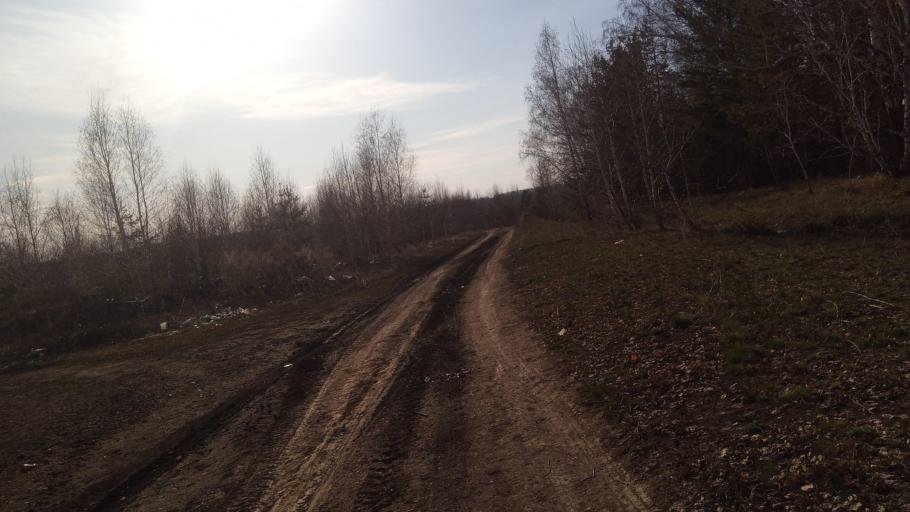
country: RU
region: Chelyabinsk
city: Sargazy
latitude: 55.1194
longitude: 61.2517
